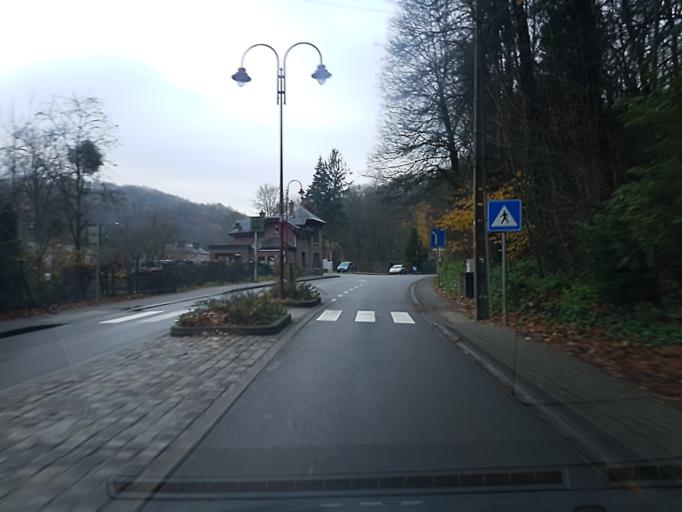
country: BE
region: Wallonia
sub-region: Province de Liege
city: Trooz
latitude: 50.5718
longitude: 5.6895
